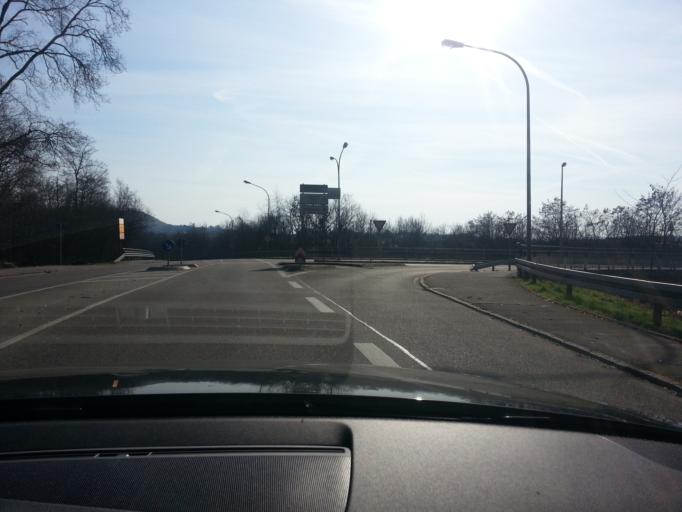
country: DE
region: Baden-Wuerttemberg
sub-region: Regierungsbezirk Stuttgart
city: Neckarsulm
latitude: 49.2059
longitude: 9.2292
